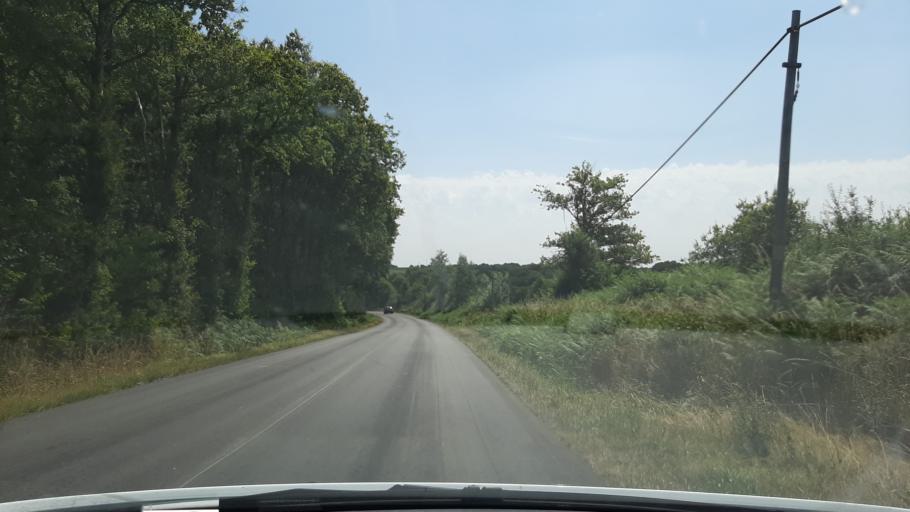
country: FR
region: Pays de la Loire
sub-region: Departement de la Vendee
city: Le Poire-sur-Vie
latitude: 46.7831
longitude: -1.5369
